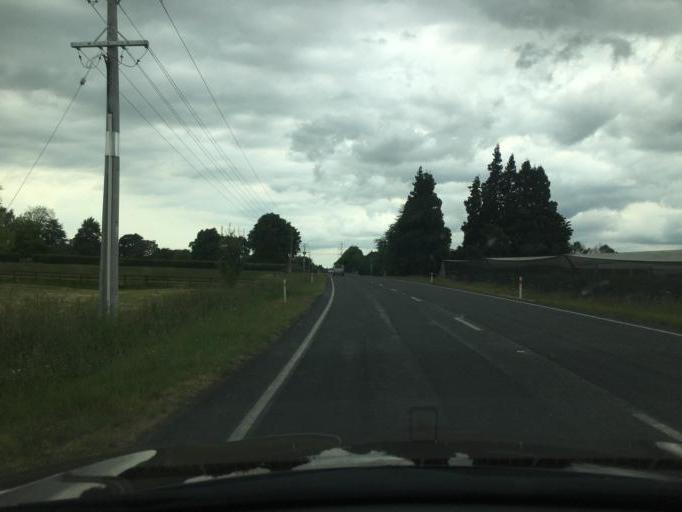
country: NZ
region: Waikato
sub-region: Waipa District
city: Cambridge
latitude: -37.9137
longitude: 175.4495
